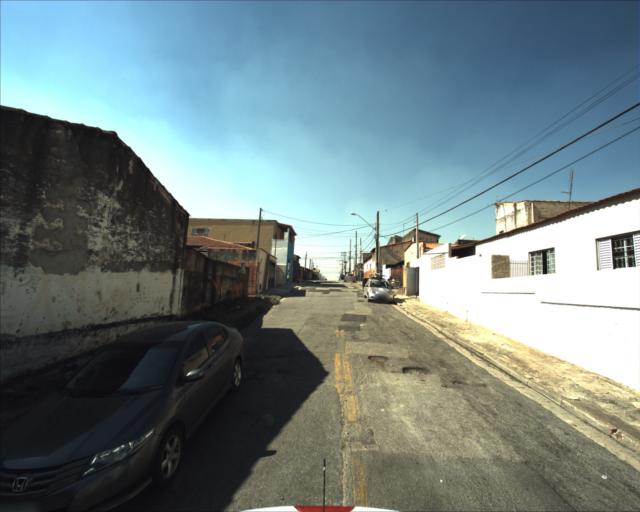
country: BR
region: Sao Paulo
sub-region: Sorocaba
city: Sorocaba
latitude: -23.4996
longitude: -47.4383
